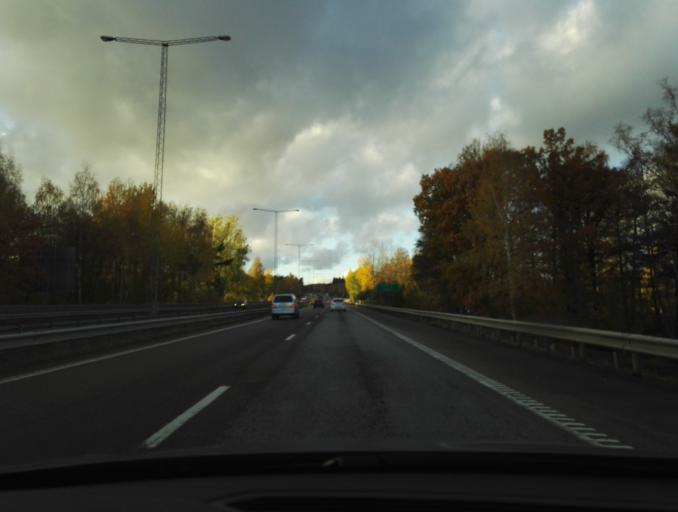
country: SE
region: Kronoberg
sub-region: Vaxjo Kommun
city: Vaexjoe
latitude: 56.8935
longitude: 14.7436
